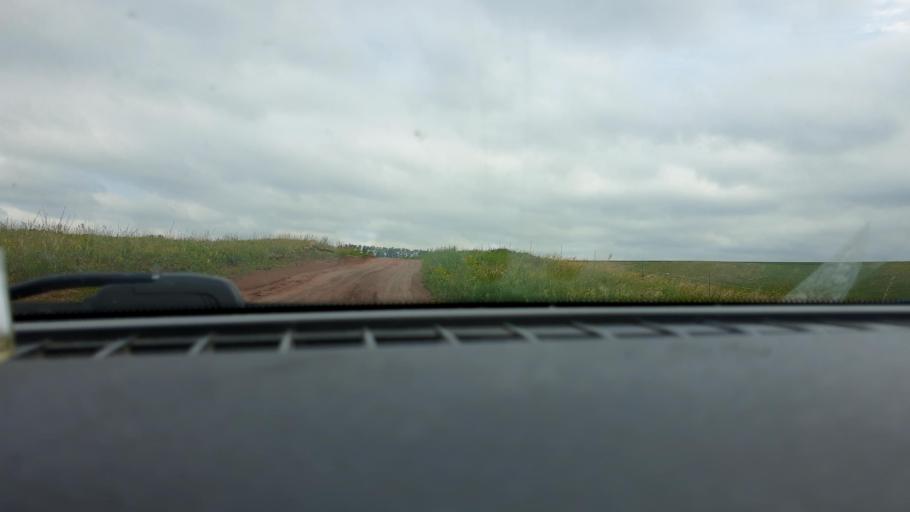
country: RU
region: Bashkortostan
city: Chishmy
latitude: 54.6900
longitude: 55.4847
